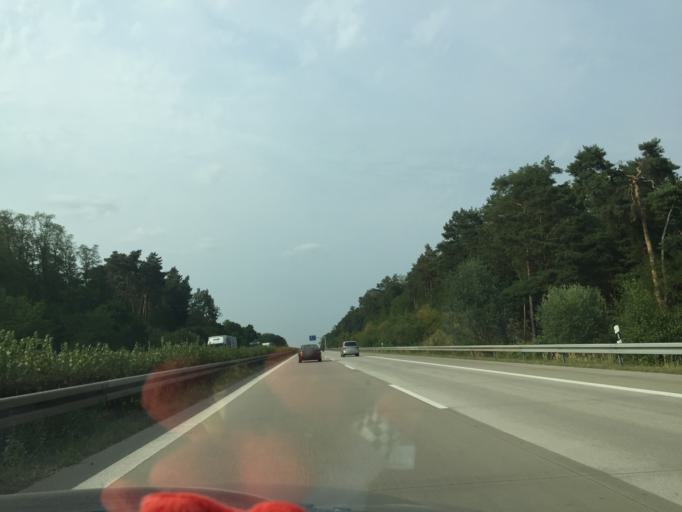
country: DE
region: Brandenburg
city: Bestensee
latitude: 52.2346
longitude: 13.5931
